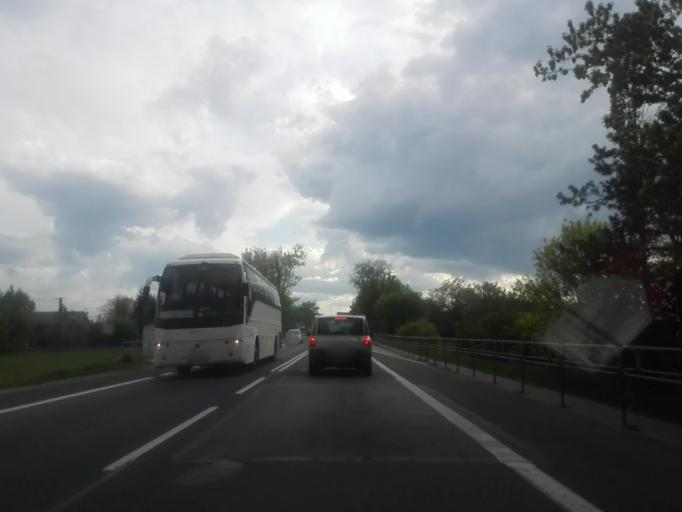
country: PL
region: Podlasie
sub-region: Powiat zambrowski
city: Szumowo
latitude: 52.8714
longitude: 22.0225
